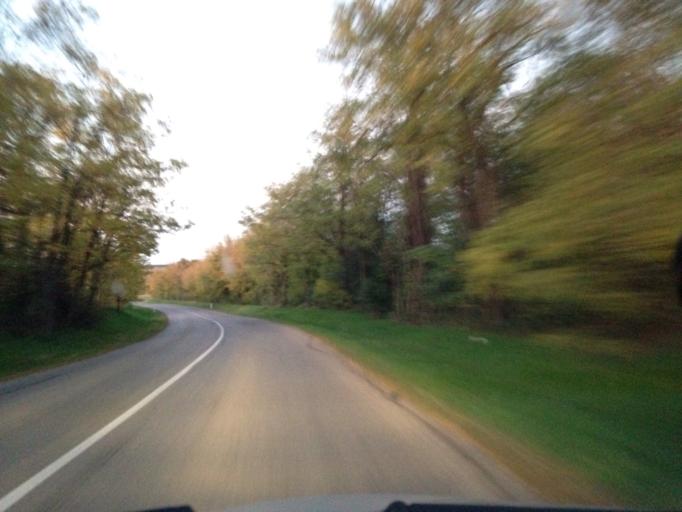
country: SK
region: Nitriansky
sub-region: Okres Komarno
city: Hurbanovo
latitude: 47.8757
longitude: 18.2853
